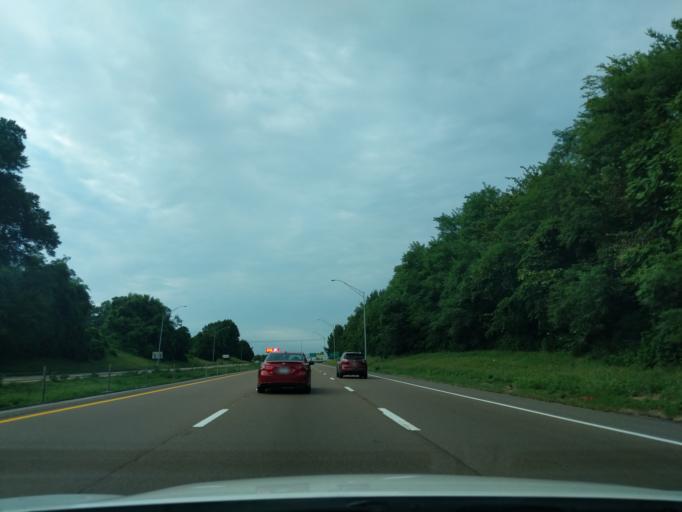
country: US
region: Tennessee
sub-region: Shelby County
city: New South Memphis
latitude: 35.1023
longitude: -90.0762
